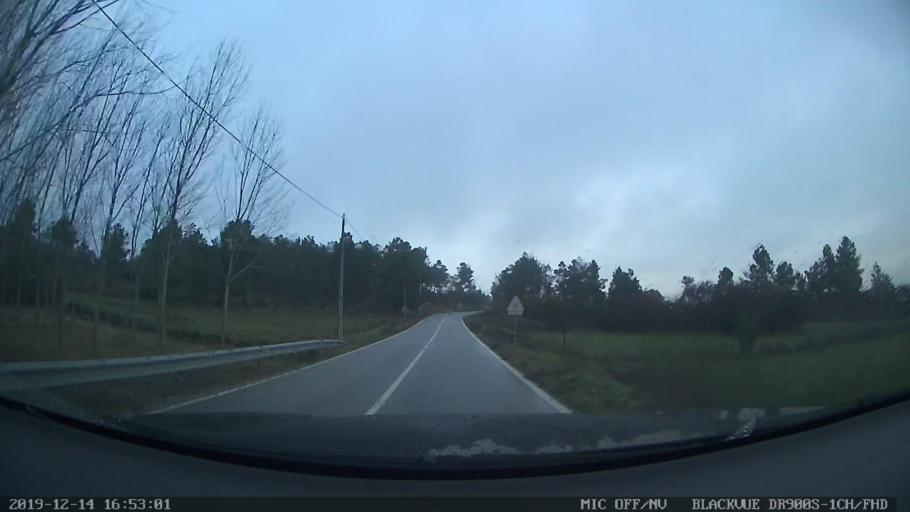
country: PT
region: Vila Real
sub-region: Murca
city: Murca
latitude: 41.4269
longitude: -7.5155
